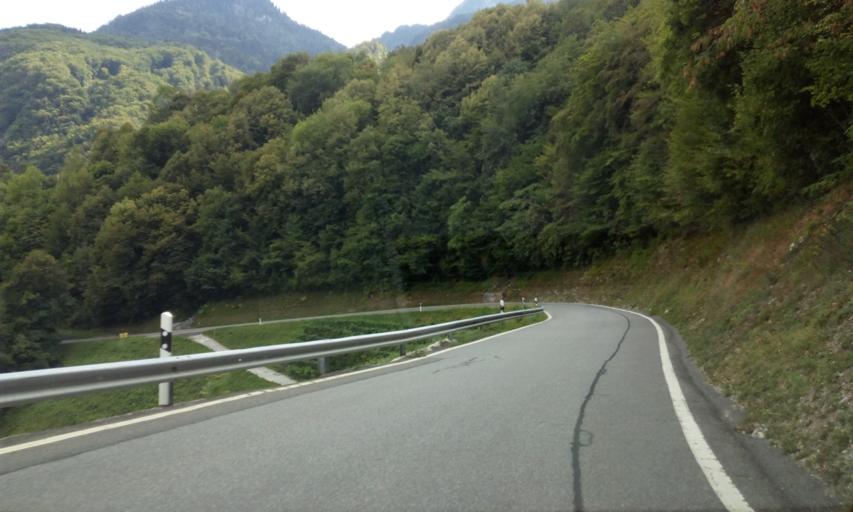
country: CH
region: Valais
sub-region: Monthey District
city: Vionnaz
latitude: 46.3115
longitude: 6.8944
